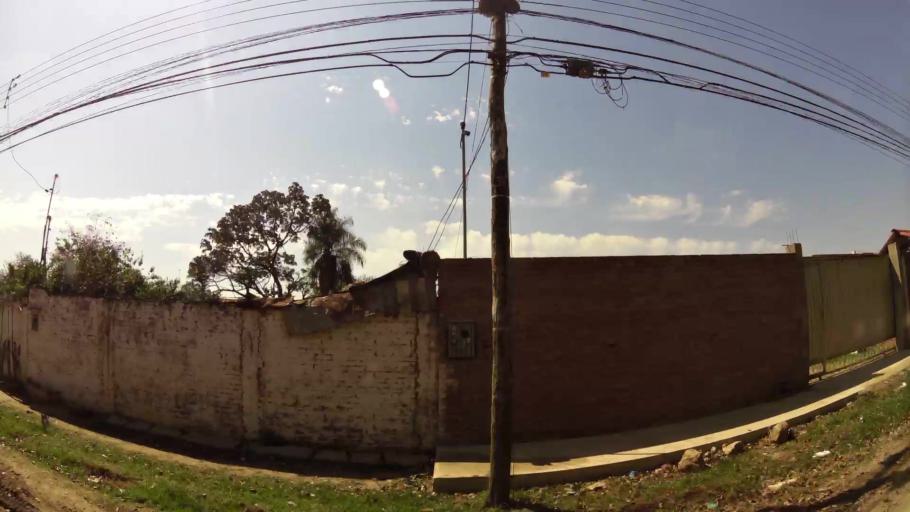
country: BO
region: Santa Cruz
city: Santa Cruz de la Sierra
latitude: -17.7332
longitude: -63.1491
